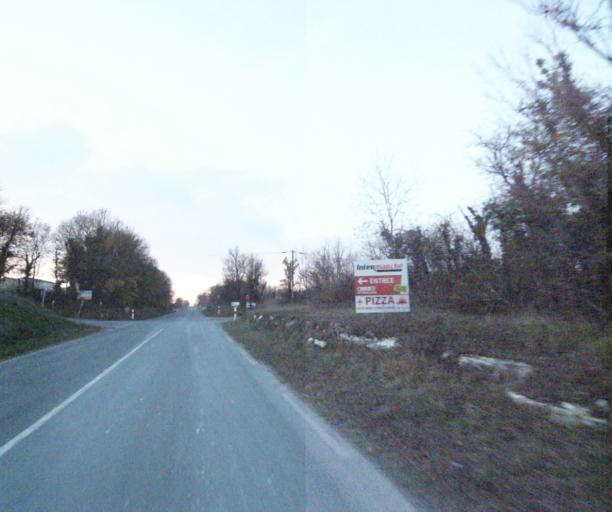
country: FR
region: Poitou-Charentes
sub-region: Departement de la Charente-Maritime
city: Saint-Porchaire
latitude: 45.8150
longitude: -0.7724
